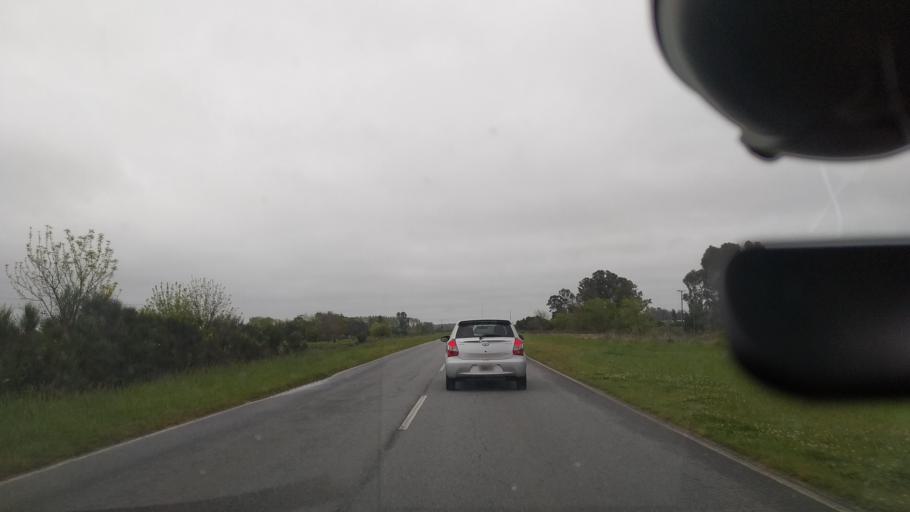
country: AR
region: Buenos Aires
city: Veronica
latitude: -35.3979
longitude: -57.3555
